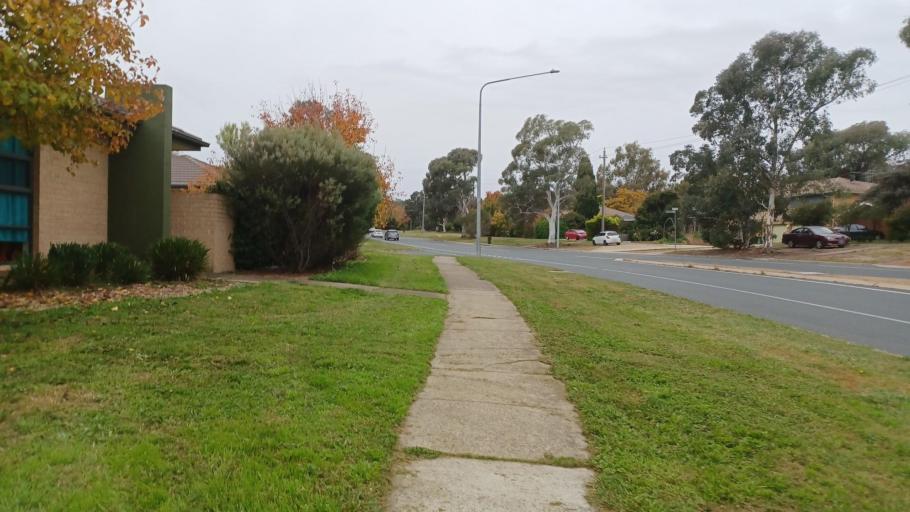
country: AU
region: Australian Capital Territory
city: Belconnen
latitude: -35.2043
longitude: 149.0388
